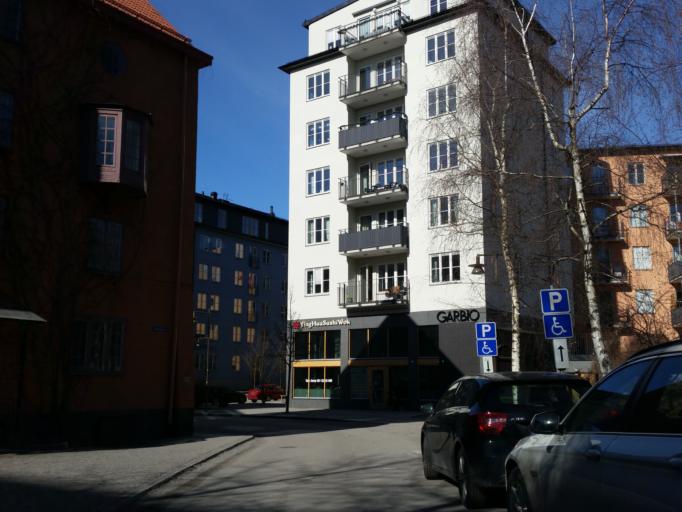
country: SE
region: Stockholm
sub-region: Solna Kommun
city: Rasunda
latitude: 59.3673
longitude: 17.9821
